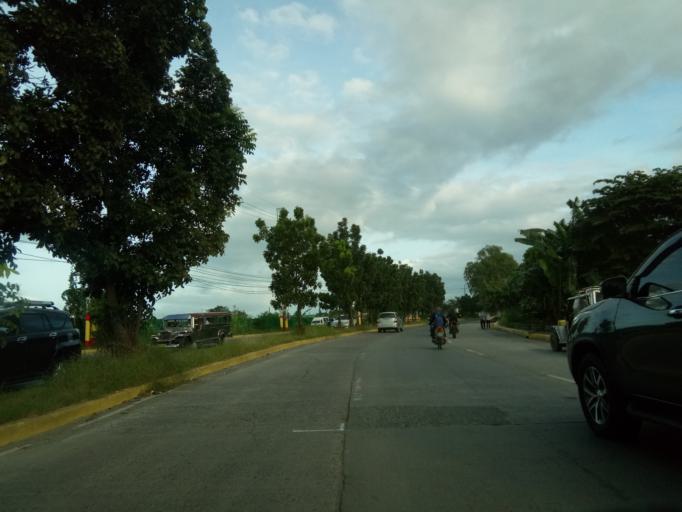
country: PH
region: Calabarzon
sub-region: Province of Cavite
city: Imus
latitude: 14.3888
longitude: 120.9681
